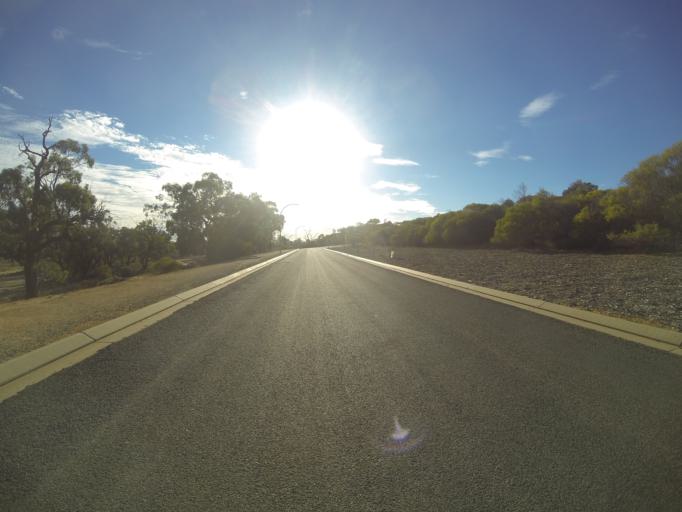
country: AU
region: South Australia
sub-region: Loxton Waikerie
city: Loxton
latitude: -34.4521
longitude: 140.5515
